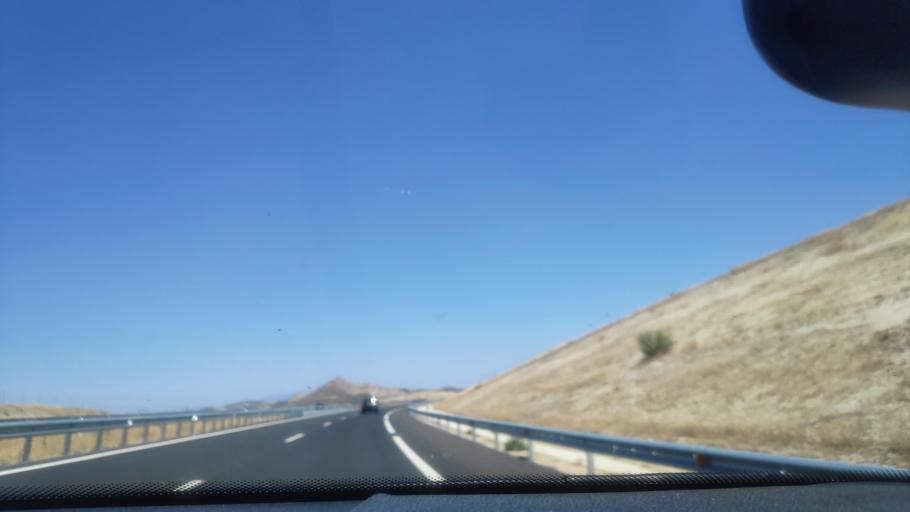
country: ES
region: Andalusia
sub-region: Provincia de Granada
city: Otura
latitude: 37.0740
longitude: -3.6609
